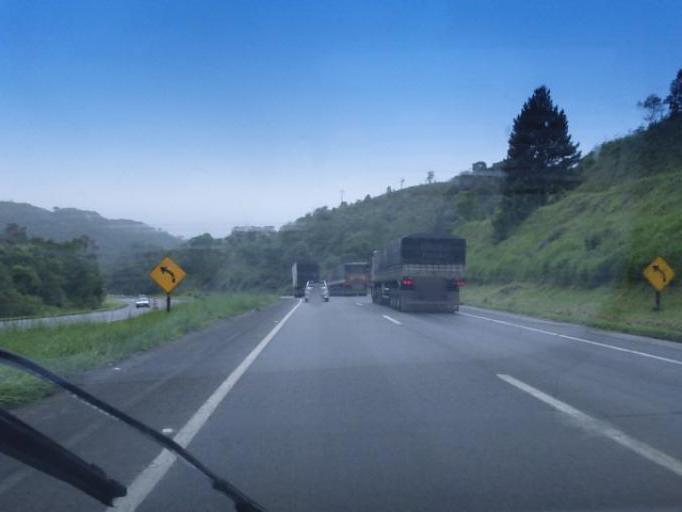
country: BR
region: Parana
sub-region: Antonina
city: Antonina
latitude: -25.0820
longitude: -48.6188
